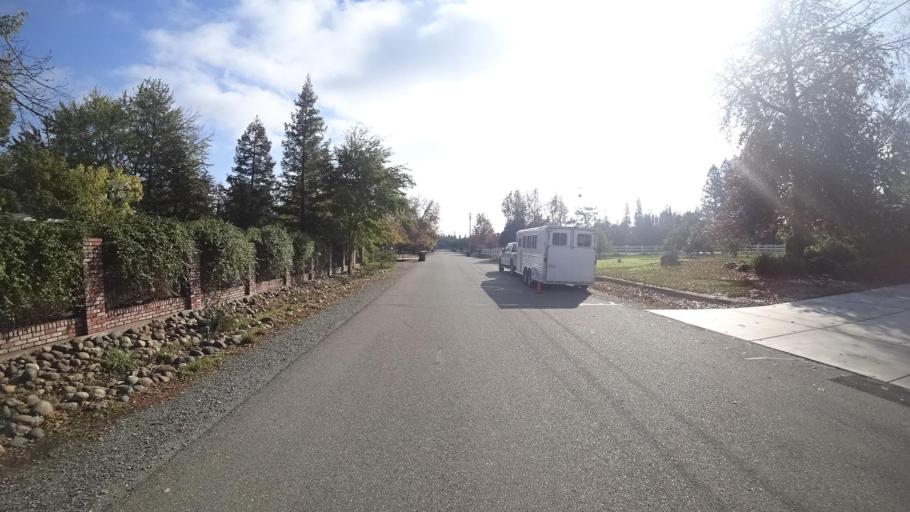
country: US
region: California
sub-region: Sacramento County
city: Vineyard
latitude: 38.4415
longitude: -121.3576
